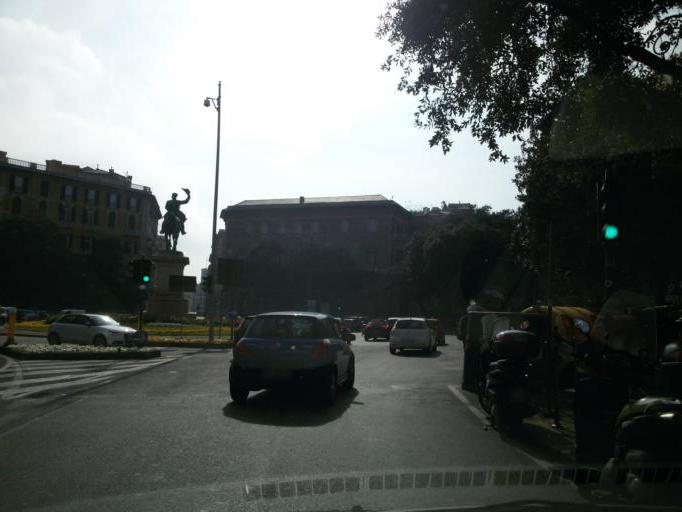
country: IT
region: Liguria
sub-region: Provincia di Genova
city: Genoa
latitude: 44.4104
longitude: 8.9389
